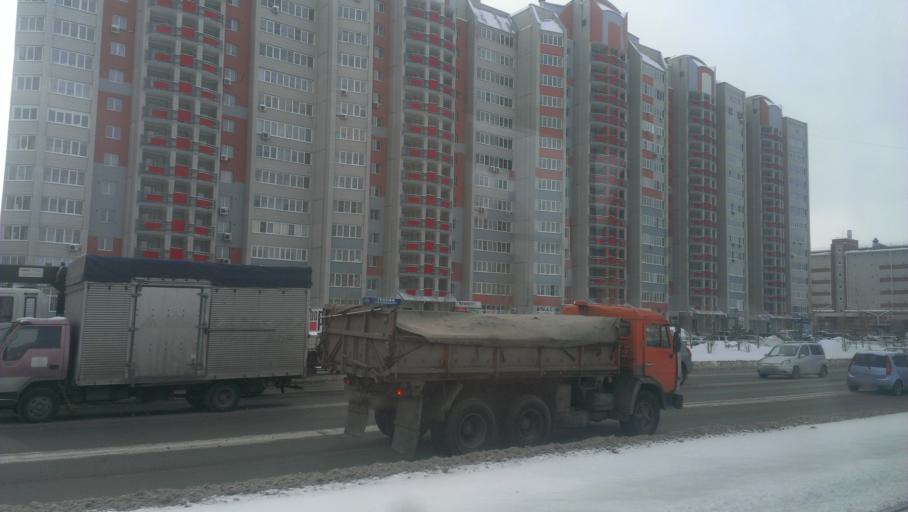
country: RU
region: Altai Krai
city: Novosilikatnyy
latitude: 53.3285
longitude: 83.6807
